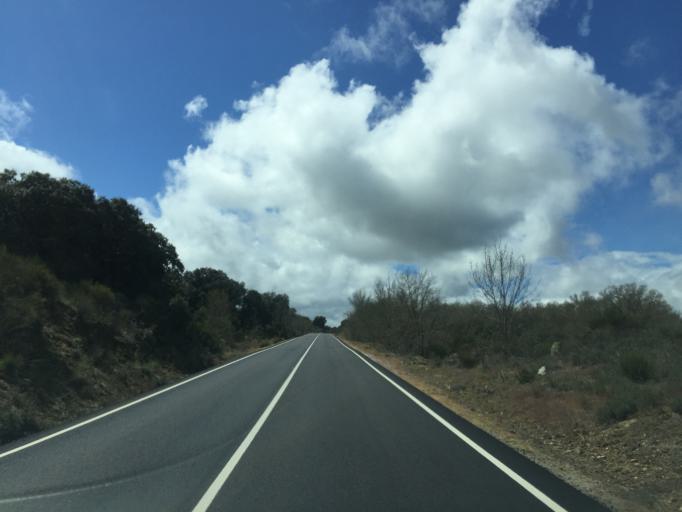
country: ES
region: Castille and Leon
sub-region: Provincia de Zamora
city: Moral de Sayago
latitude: 41.4889
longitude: -6.0968
